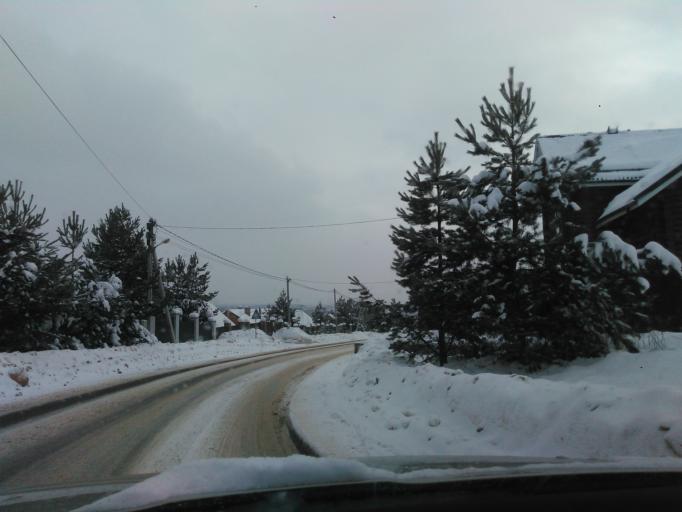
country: RU
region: Moskovskaya
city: Yakhroma
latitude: 56.2753
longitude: 37.4843
